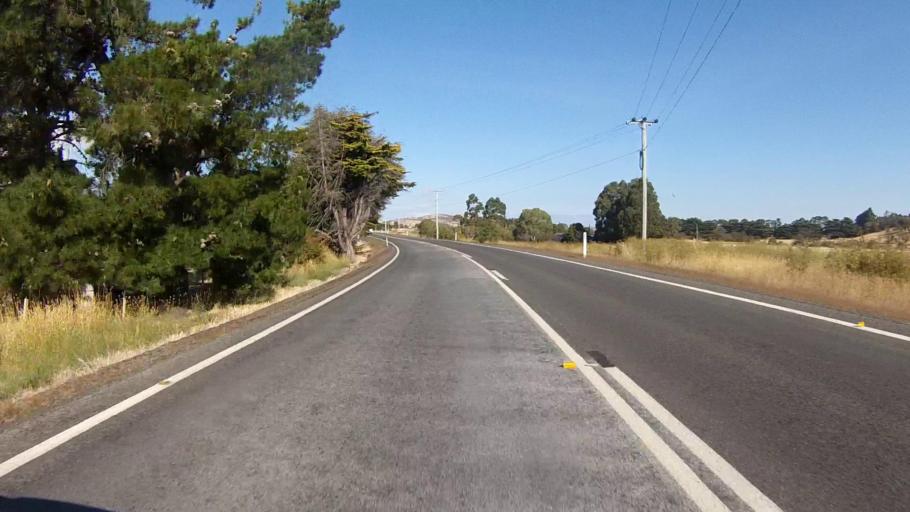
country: AU
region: Tasmania
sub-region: Sorell
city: Sorell
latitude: -42.7273
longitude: 147.5231
